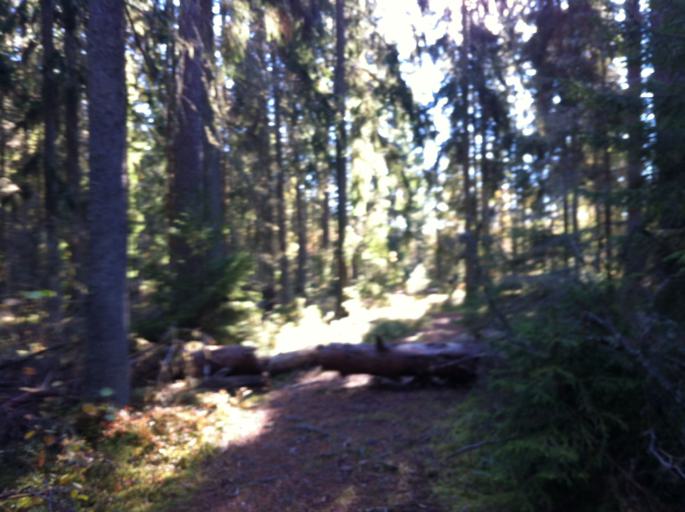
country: SE
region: Uppsala
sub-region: Heby Kommun
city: Tarnsjo
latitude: 60.2309
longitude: 16.9571
